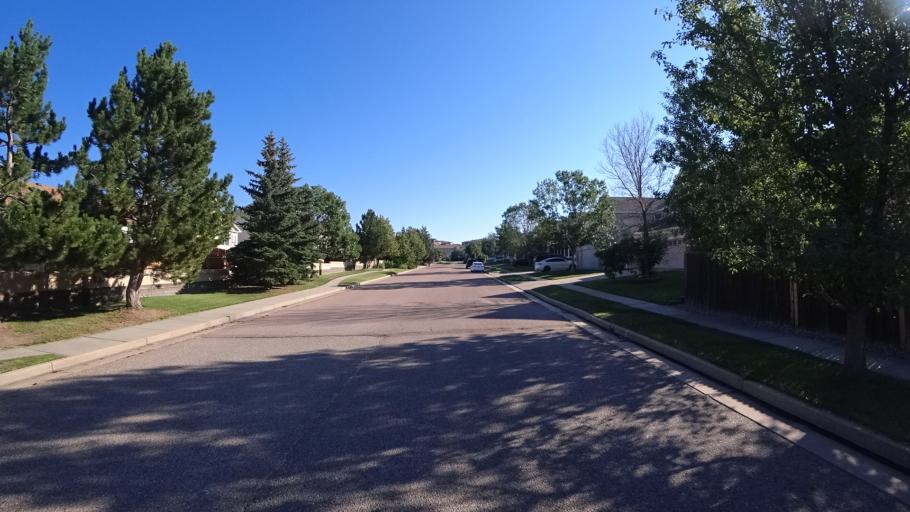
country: US
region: Colorado
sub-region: El Paso County
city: Black Forest
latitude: 38.9623
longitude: -104.7446
